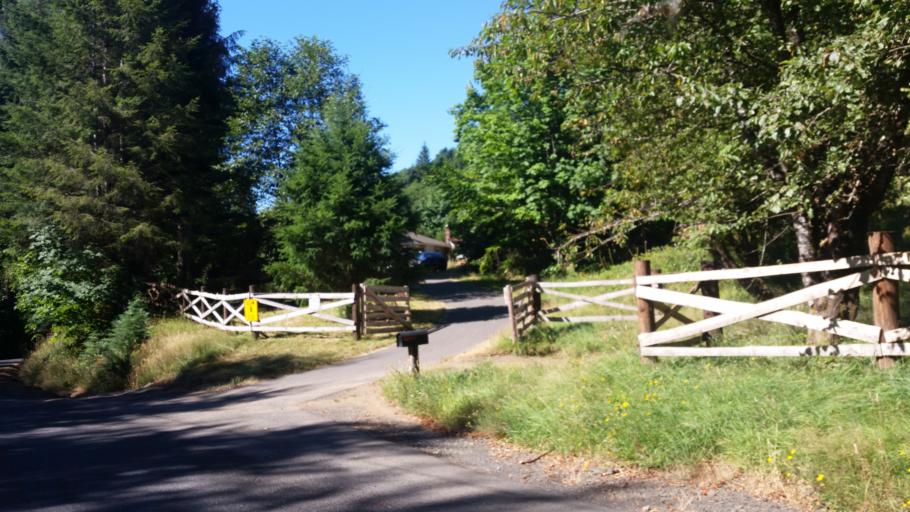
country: US
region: Washington
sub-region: Clark County
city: Amboy
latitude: 46.0028
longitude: -122.5304
